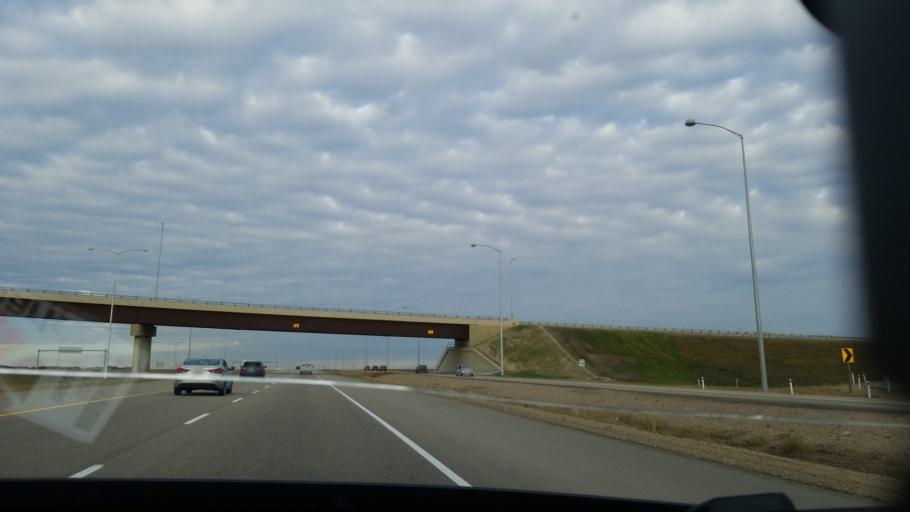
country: CA
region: Alberta
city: Edmonton
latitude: 53.6360
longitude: -113.3961
